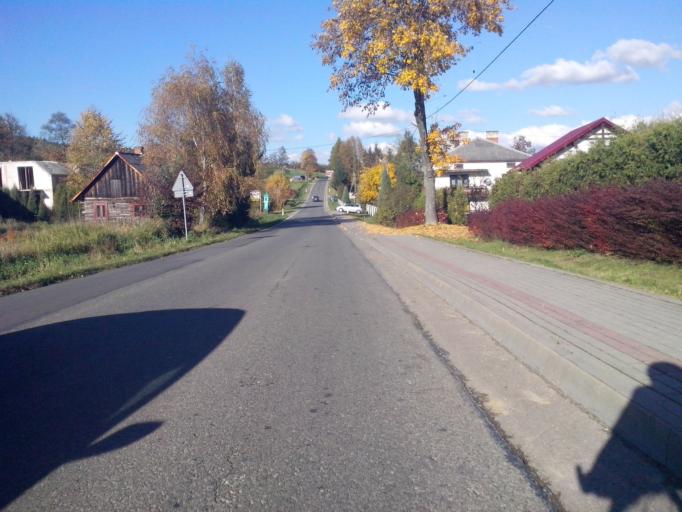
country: PL
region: Subcarpathian Voivodeship
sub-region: Powiat strzyzowski
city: Jawornik
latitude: 49.7834
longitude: 21.8557
